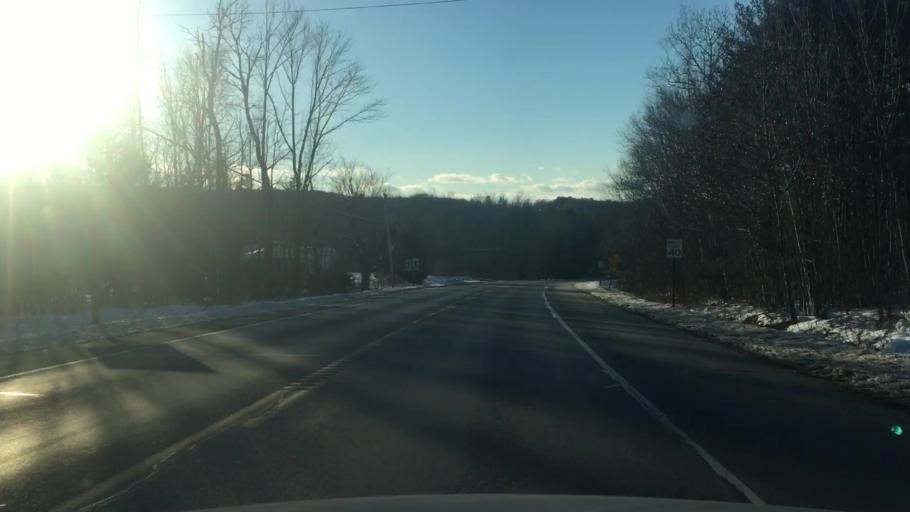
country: US
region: Maine
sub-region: Franklin County
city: New Sharon
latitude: 44.6367
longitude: -70.0019
